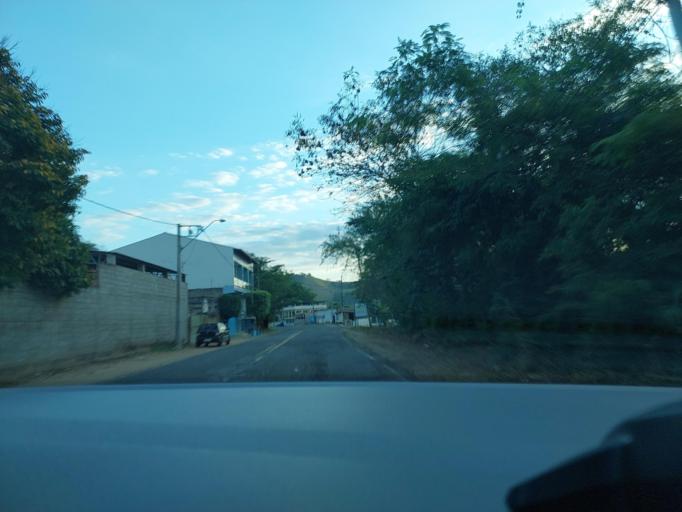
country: BR
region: Rio de Janeiro
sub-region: Natividade
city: Natividade
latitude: -21.2001
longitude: -42.1226
